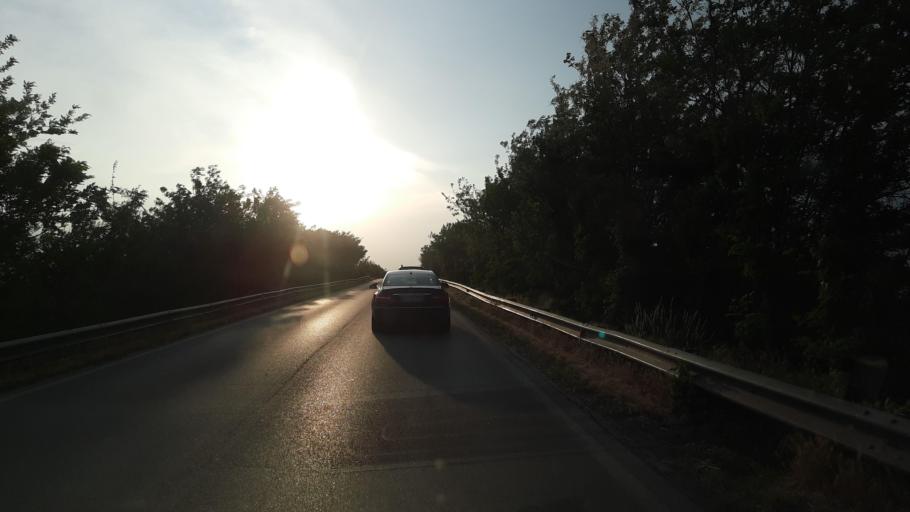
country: IT
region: Lombardy
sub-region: Provincia di Pavia
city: Mortara
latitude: 45.2456
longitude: 8.7314
